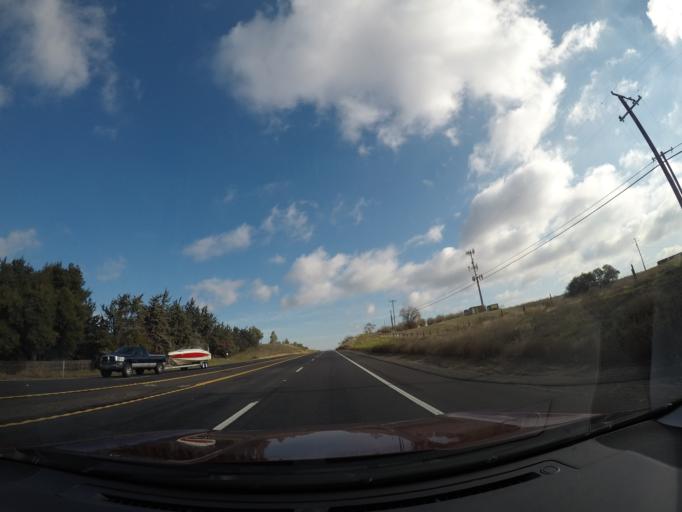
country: US
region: California
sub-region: Stanislaus County
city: East Oakdale
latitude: 37.7828
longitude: -120.7495
